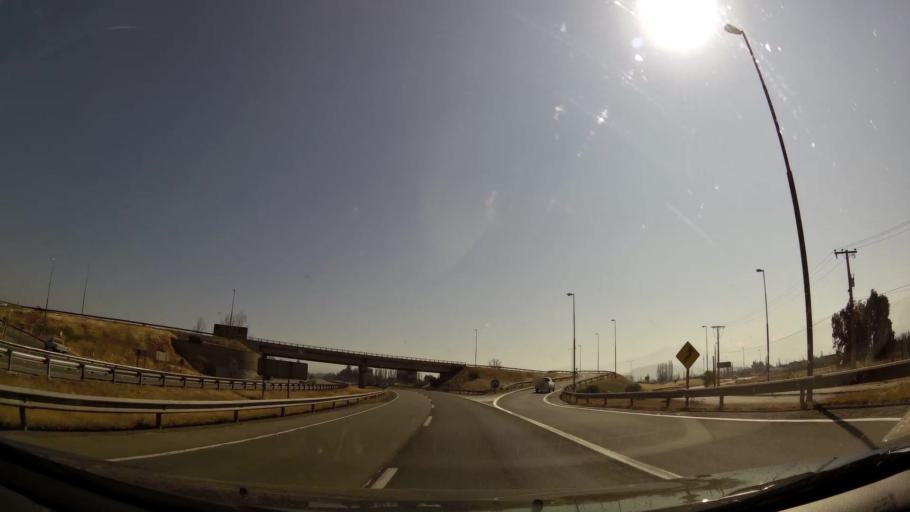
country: CL
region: Santiago Metropolitan
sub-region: Provincia de Chacabuco
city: Chicureo Abajo
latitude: -33.3058
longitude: -70.6992
